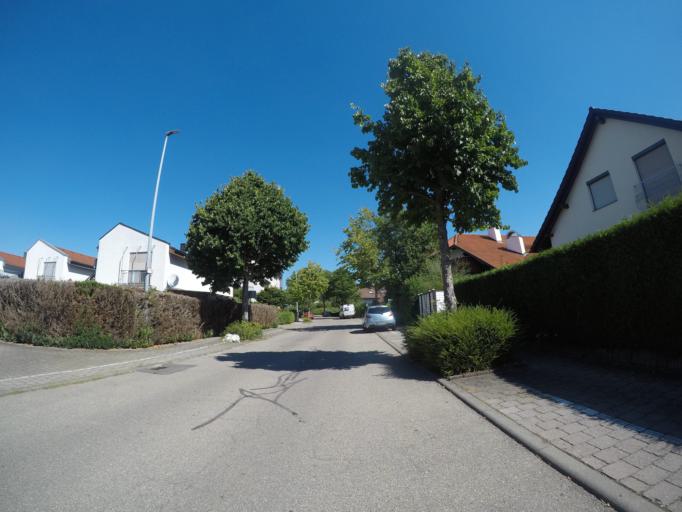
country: DE
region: Baden-Wuerttemberg
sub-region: Tuebingen Region
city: Dornstadt
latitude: 48.4609
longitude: 9.9457
